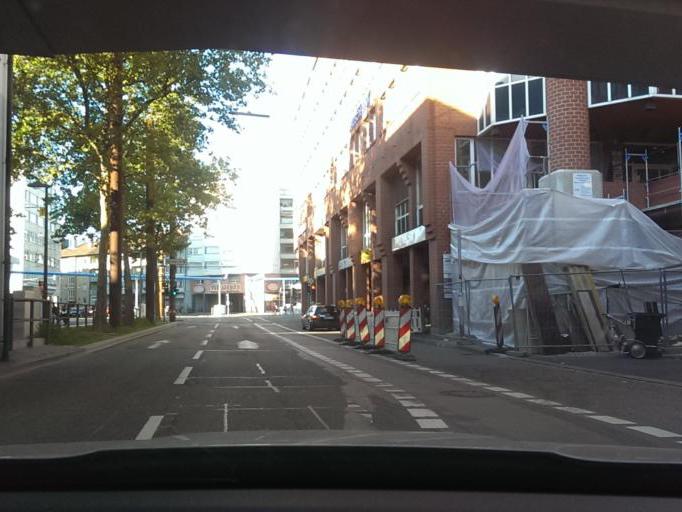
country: DE
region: Baden-Wuerttemberg
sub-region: Karlsruhe Region
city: Karlsruhe
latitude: 49.0086
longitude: 8.4102
